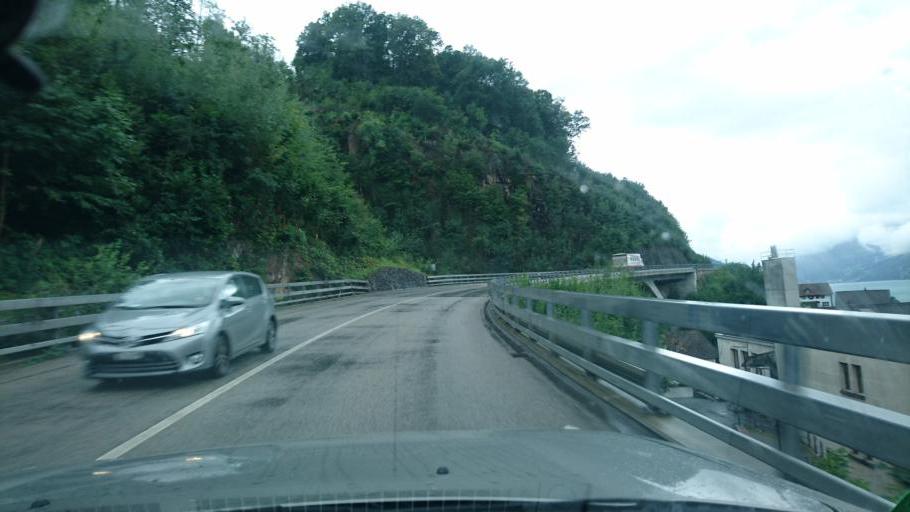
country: CH
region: Saint Gallen
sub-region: Wahlkreis Sarganserland
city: Quarten
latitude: 47.1118
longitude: 9.2173
